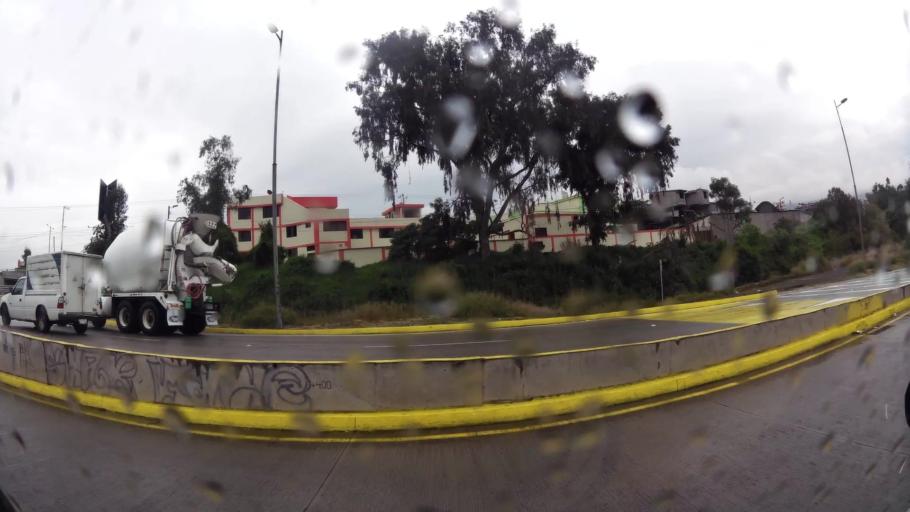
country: EC
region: Pichincha
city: Sangolqui
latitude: -0.2920
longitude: -78.4633
